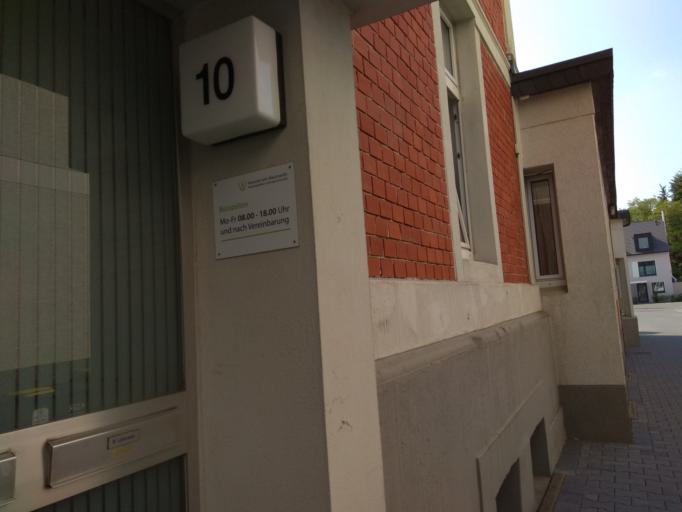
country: DE
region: North Rhine-Westphalia
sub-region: Regierungsbezirk Arnsberg
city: Herne
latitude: 51.5719
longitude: 7.2138
